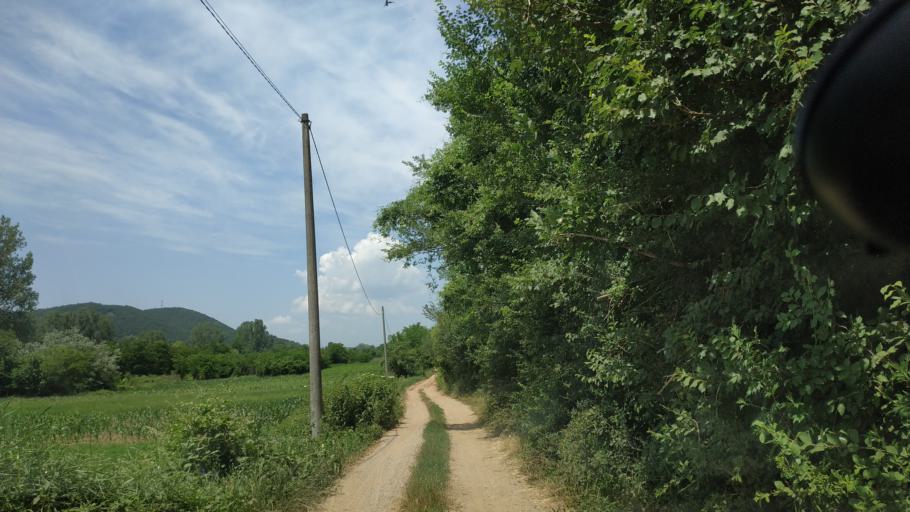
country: RS
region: Central Serbia
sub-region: Nisavski Okrug
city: Aleksinac
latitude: 43.5724
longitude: 21.7044
